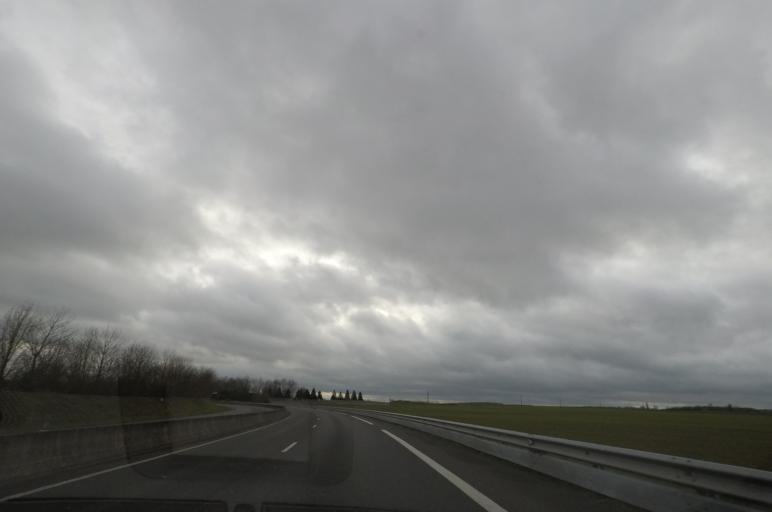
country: FR
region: Centre
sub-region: Departement du Loir-et-Cher
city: Saint-Sulpice-de-Pommeray
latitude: 47.6689
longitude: 1.2326
